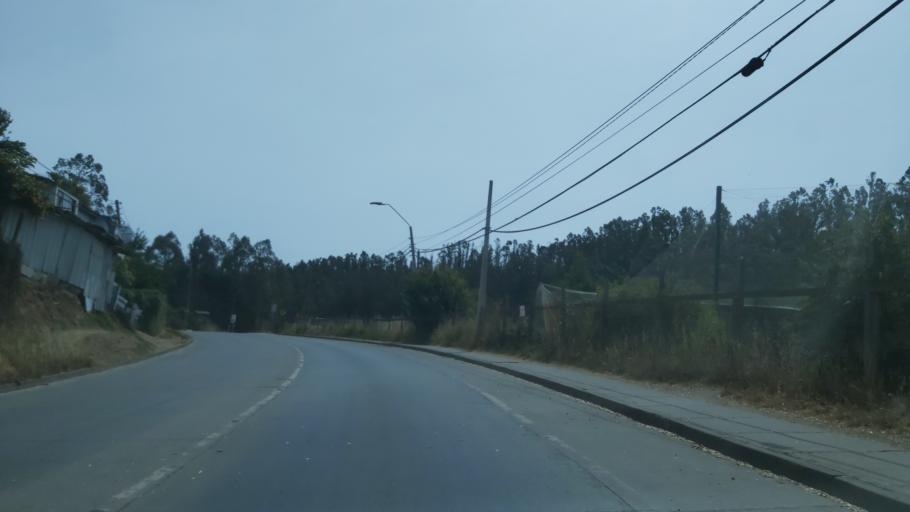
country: CL
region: Maule
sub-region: Provincia de Talca
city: Constitucion
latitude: -35.3376
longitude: -72.4185
